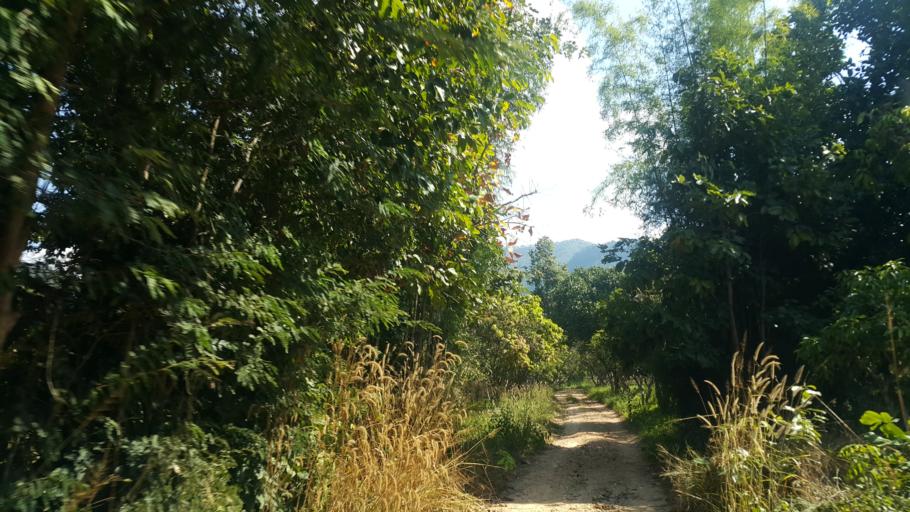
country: TH
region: Lamphun
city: Ban Thi
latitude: 18.6710
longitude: 99.1829
